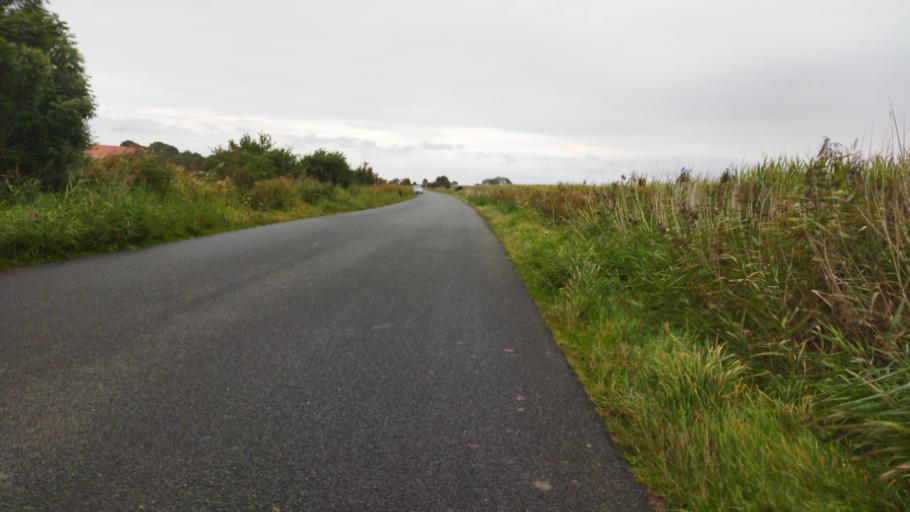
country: DE
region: Lower Saxony
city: Wirdum
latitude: 53.4978
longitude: 7.0580
